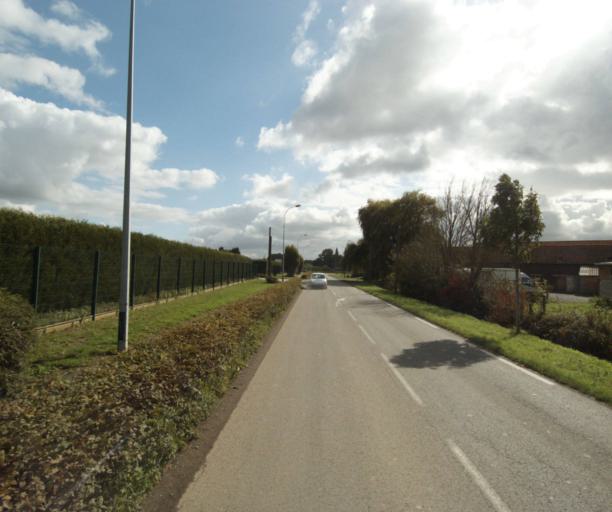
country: FR
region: Nord-Pas-de-Calais
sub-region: Departement du Nord
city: Deulemont
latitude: 50.7251
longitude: 2.9456
